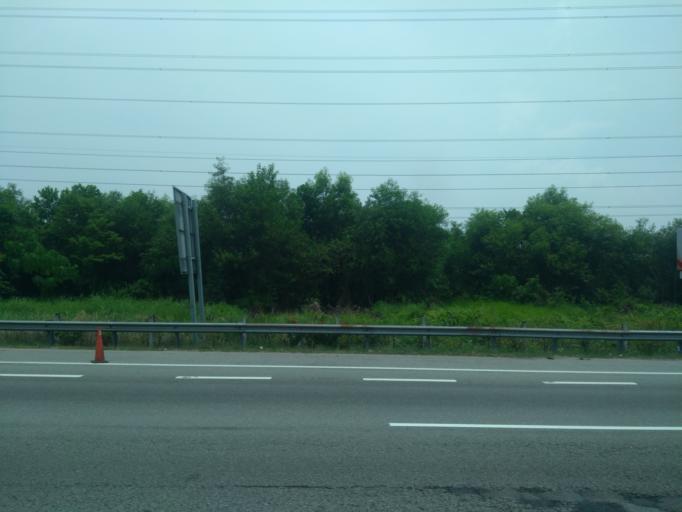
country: MY
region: Penang
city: Juru
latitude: 5.2831
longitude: 100.4525
